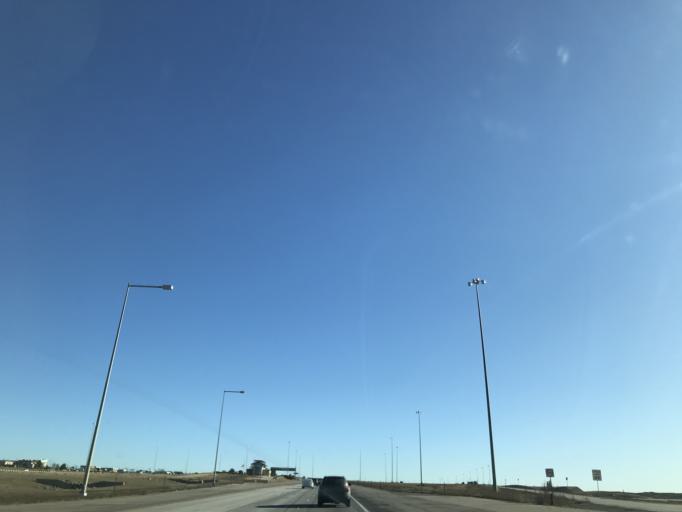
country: US
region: Colorado
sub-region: Adams County
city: Aurora
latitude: 39.8330
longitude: -104.7279
